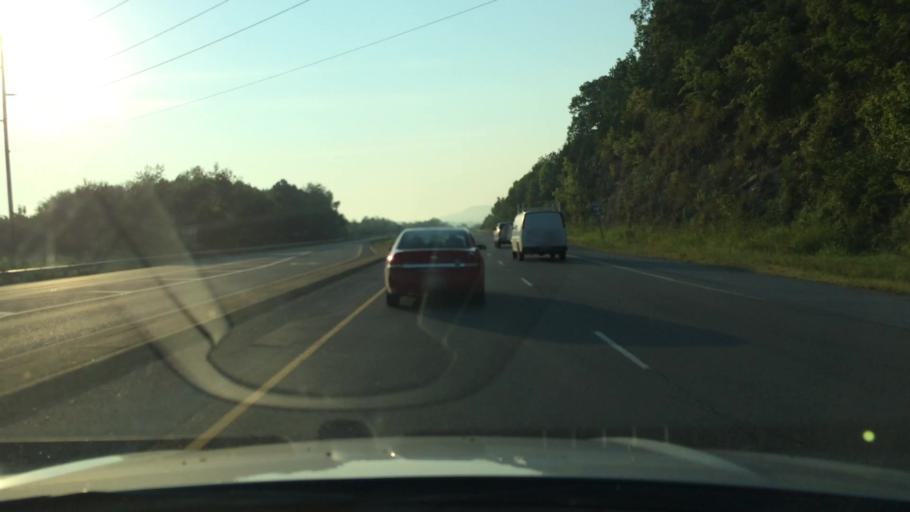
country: US
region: Tennessee
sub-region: Giles County
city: Pulaski
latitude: 35.1701
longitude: -87.0512
